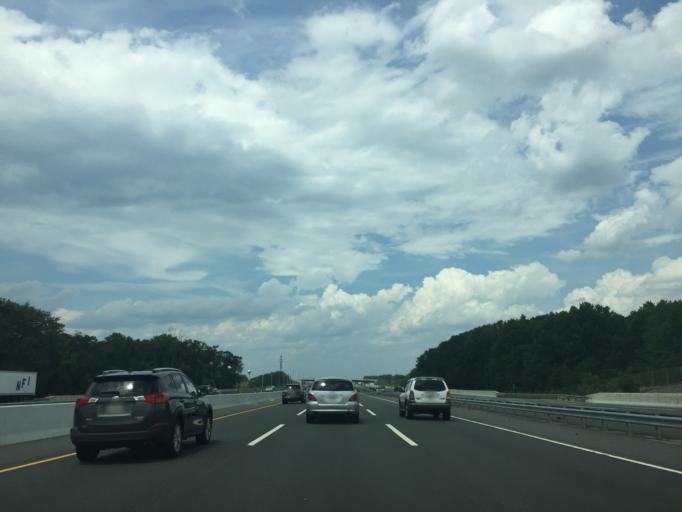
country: US
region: New Jersey
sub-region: Middlesex County
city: Cranbury
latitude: 40.3064
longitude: -74.4929
